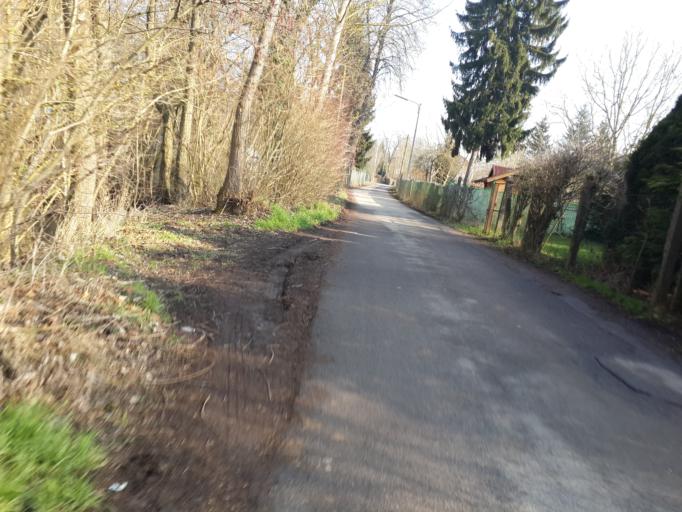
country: DE
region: Baden-Wuerttemberg
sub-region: Regierungsbezirk Stuttgart
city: Heilbronn
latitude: 49.1661
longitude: 9.1916
